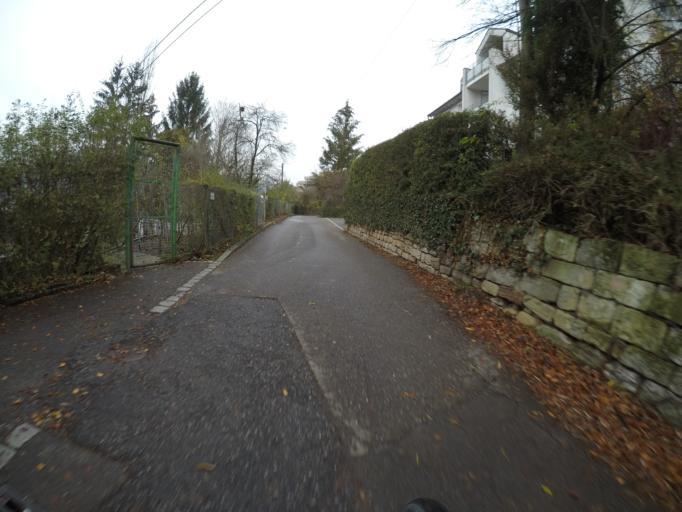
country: DE
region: Baden-Wuerttemberg
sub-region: Regierungsbezirk Stuttgart
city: Stuttgart
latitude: 48.7580
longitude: 9.1644
